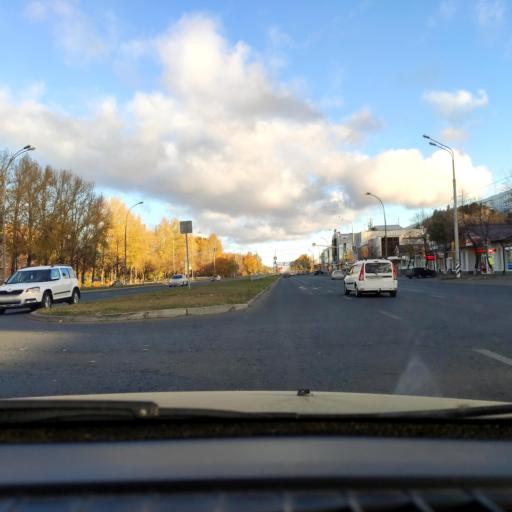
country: RU
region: Samara
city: Tol'yatti
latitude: 53.5340
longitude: 49.2829
